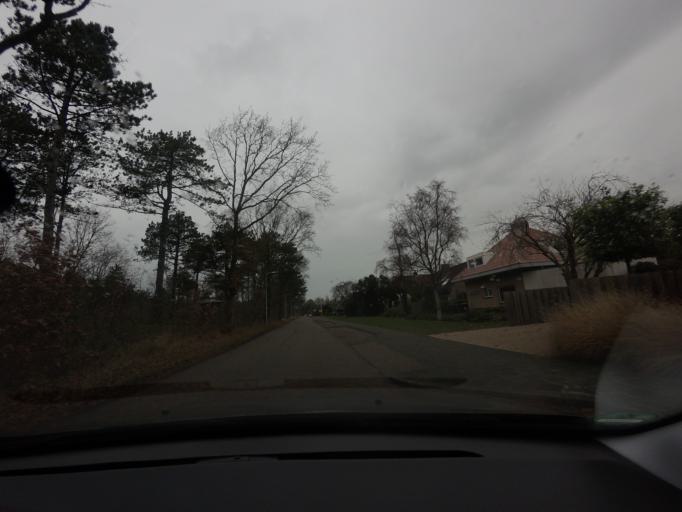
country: NL
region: North Holland
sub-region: Gemeente Texel
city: Den Burg
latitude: 53.0916
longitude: 4.7581
